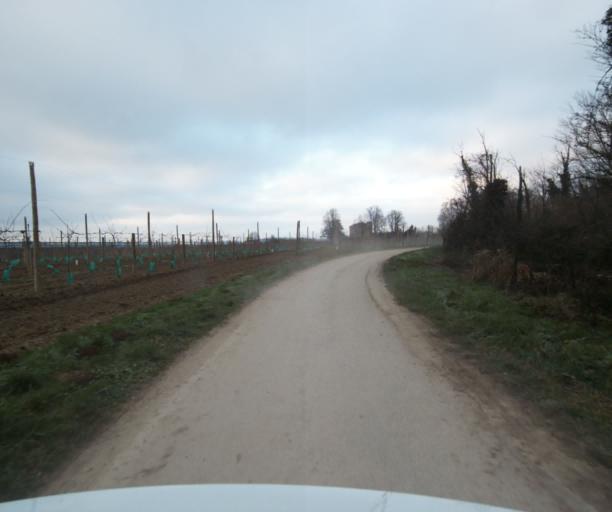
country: FR
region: Midi-Pyrenees
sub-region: Departement du Tarn-et-Garonne
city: Moissac
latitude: 44.0940
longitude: 1.1261
